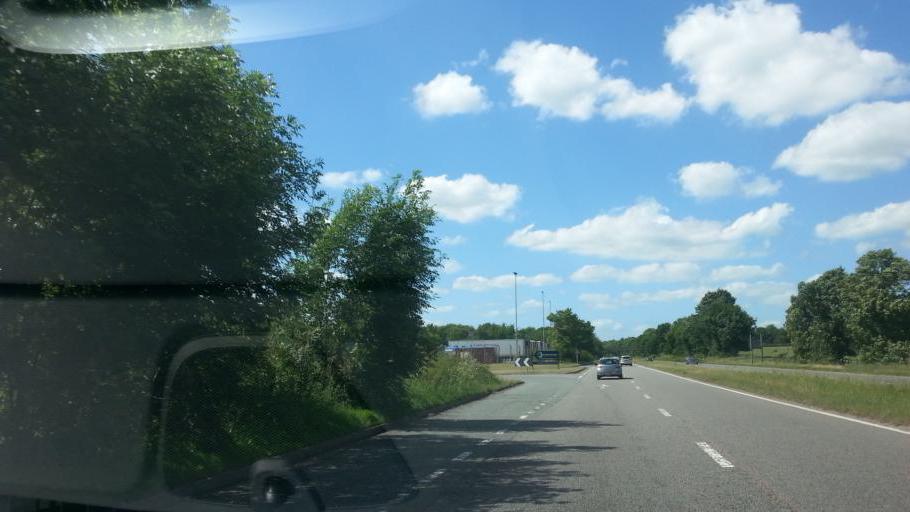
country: GB
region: England
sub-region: Hertfordshire
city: Shenley AV
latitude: 51.7223
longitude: -0.2860
